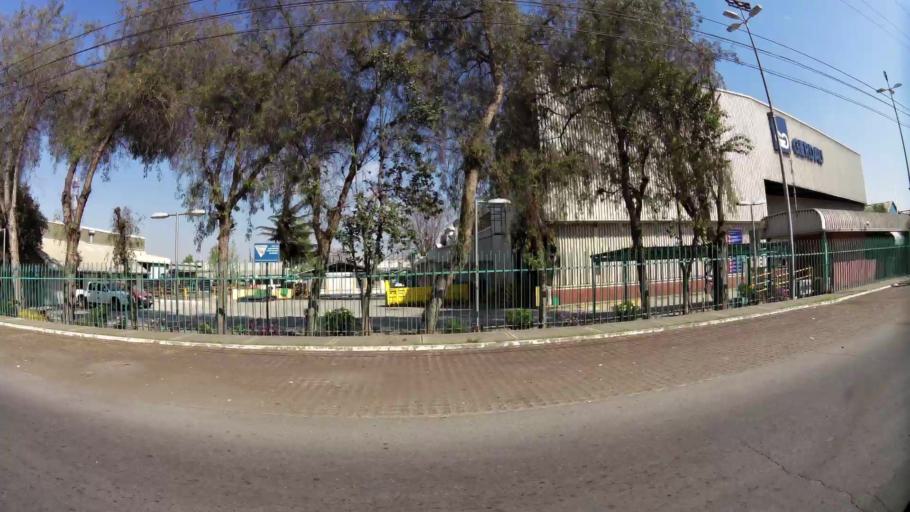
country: CL
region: Santiago Metropolitan
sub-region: Provincia de Santiago
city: Lo Prado
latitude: -33.4016
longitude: -70.6837
